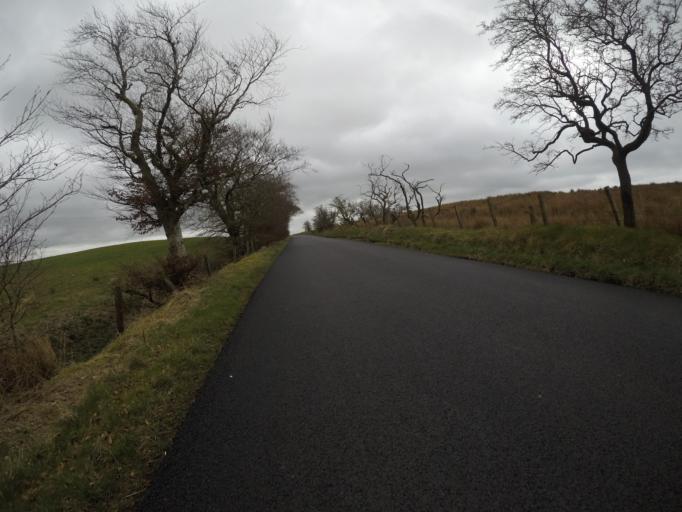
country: GB
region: Scotland
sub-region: East Ayrshire
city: Stewarton
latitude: 55.6818
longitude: -4.4601
